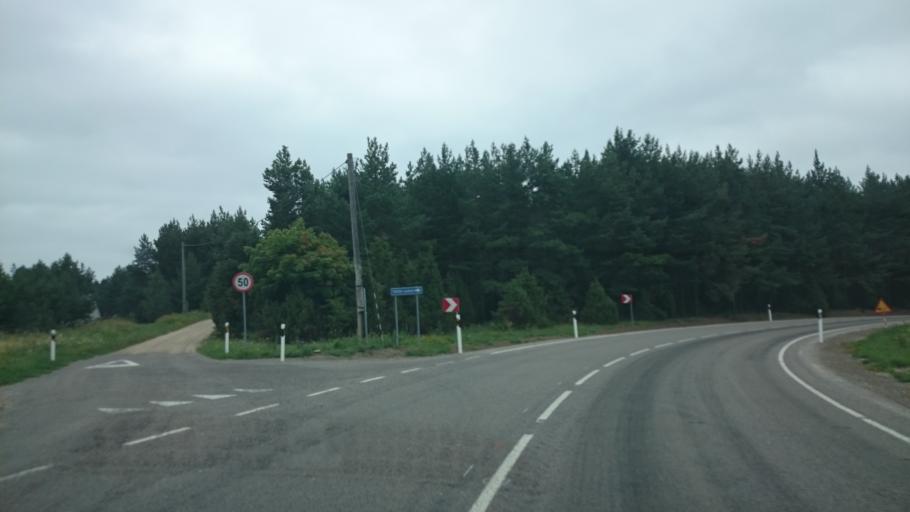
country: EE
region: Saare
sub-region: Orissaare vald
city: Orissaare
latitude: 58.5879
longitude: 22.7055
